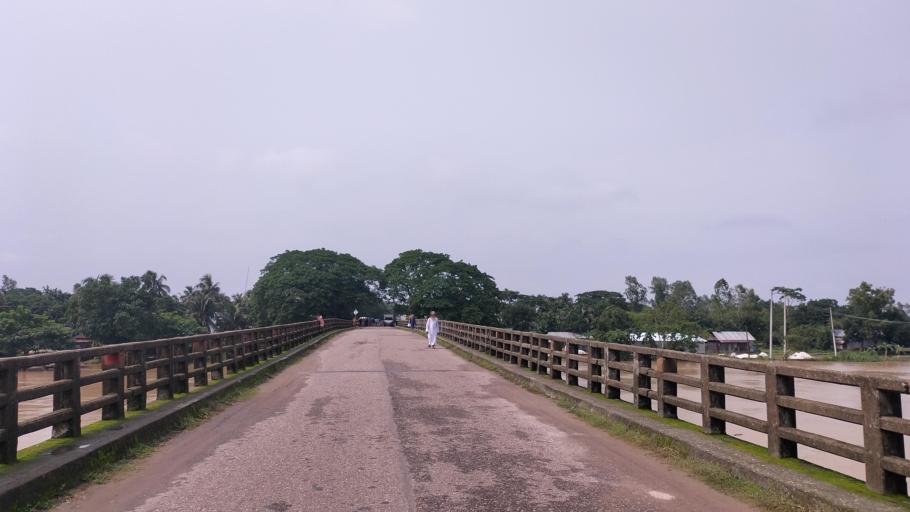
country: BD
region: Dhaka
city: Netrakona
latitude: 24.9537
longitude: 90.8341
